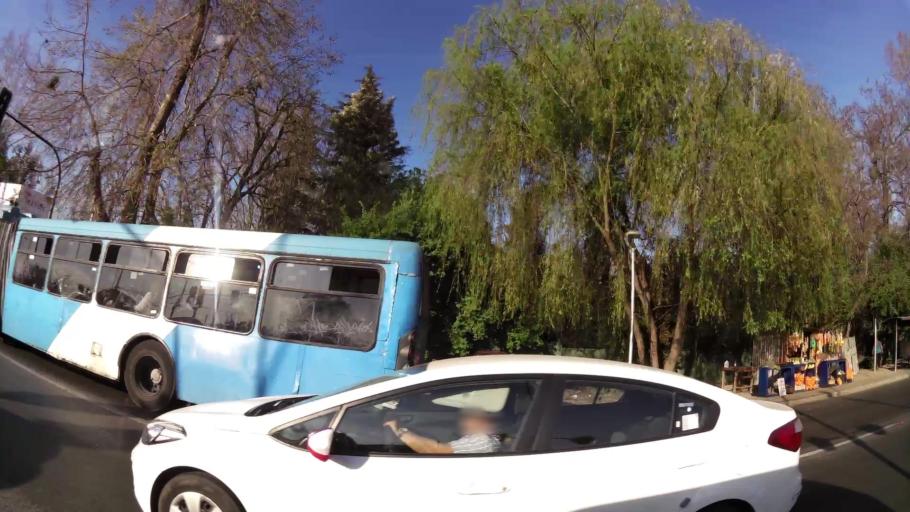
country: CL
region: Santiago Metropolitan
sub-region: Provincia de Santiago
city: Villa Presidente Frei, Nunoa, Santiago, Chile
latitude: -33.5288
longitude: -70.5761
